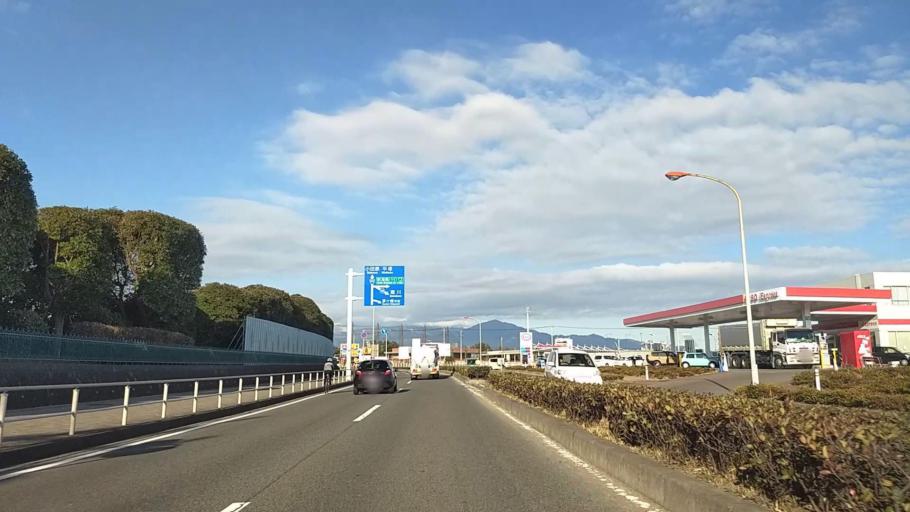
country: JP
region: Kanagawa
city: Chigasaki
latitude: 35.3193
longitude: 139.3790
